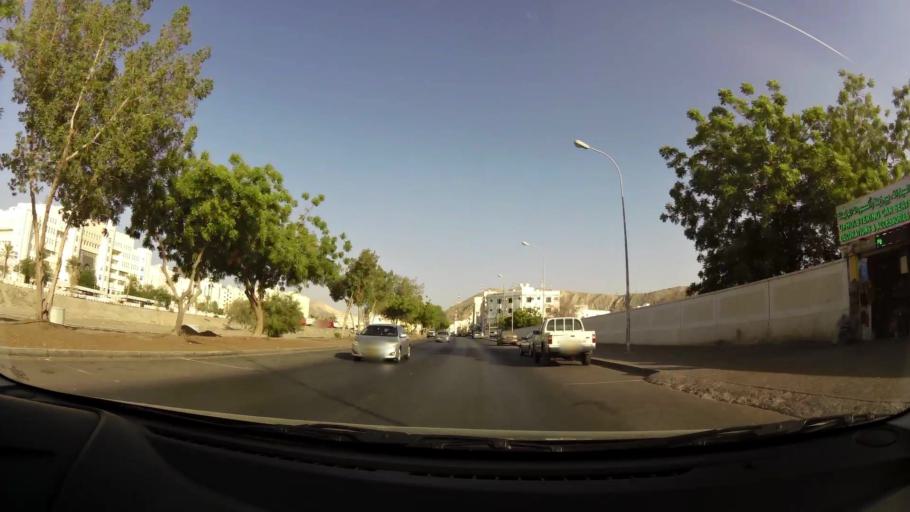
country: OM
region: Muhafazat Masqat
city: Muscat
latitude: 23.5915
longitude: 58.5495
